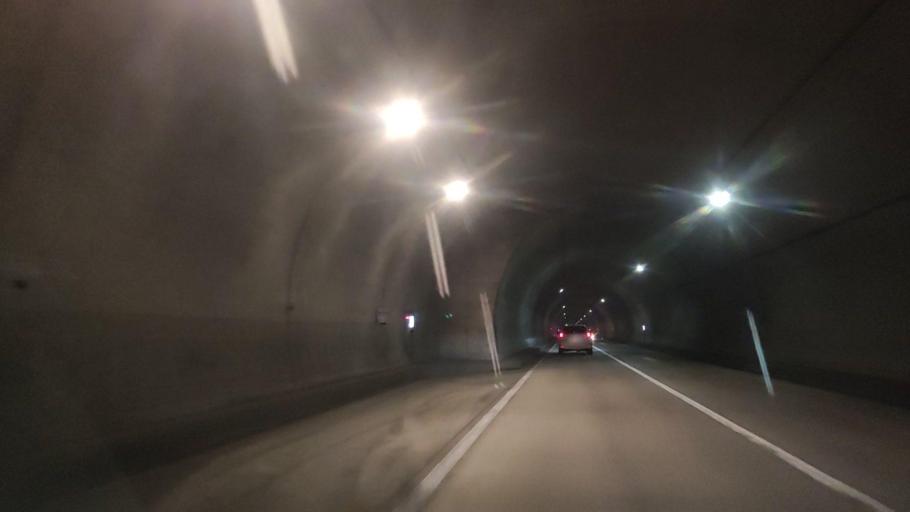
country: JP
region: Hokkaido
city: Ishikari
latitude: 43.5353
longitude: 141.3931
